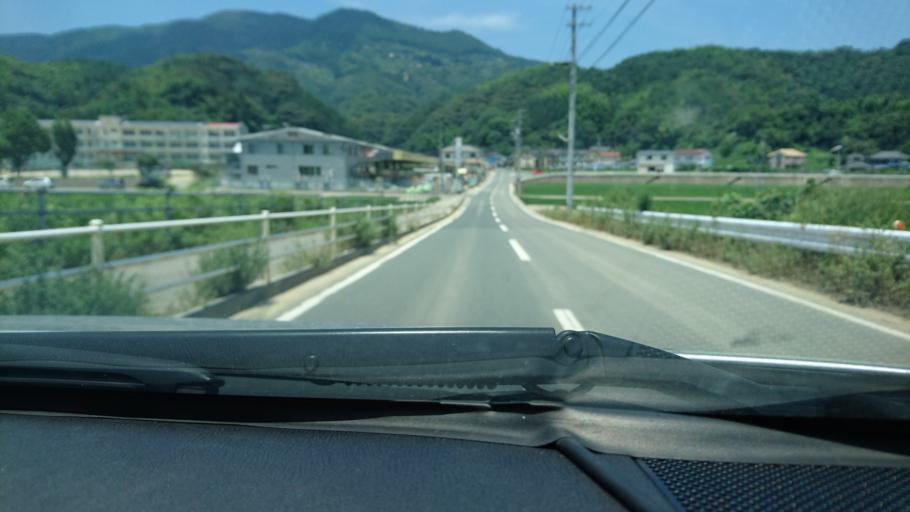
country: JP
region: Ehime
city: Ozu
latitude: 33.5070
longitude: 132.5293
